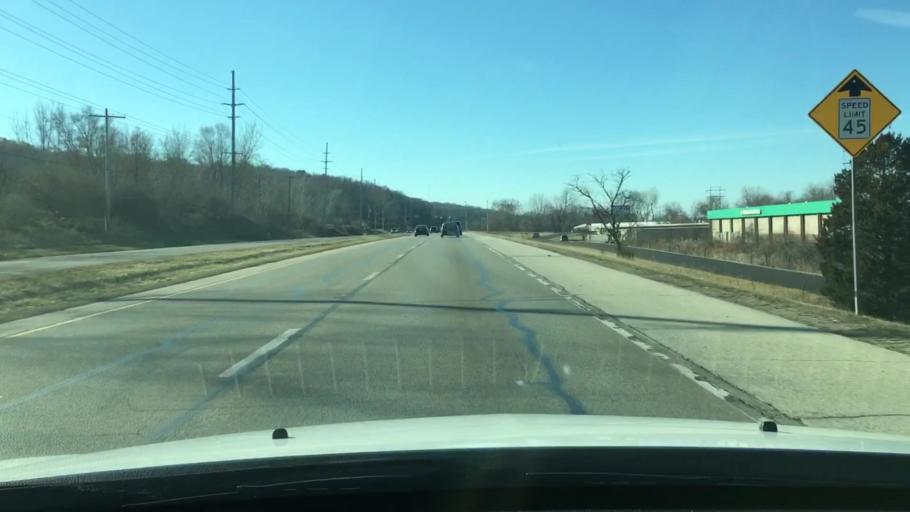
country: US
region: Illinois
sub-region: Tazewell County
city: East Peoria
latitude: 40.6855
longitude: -89.5509
